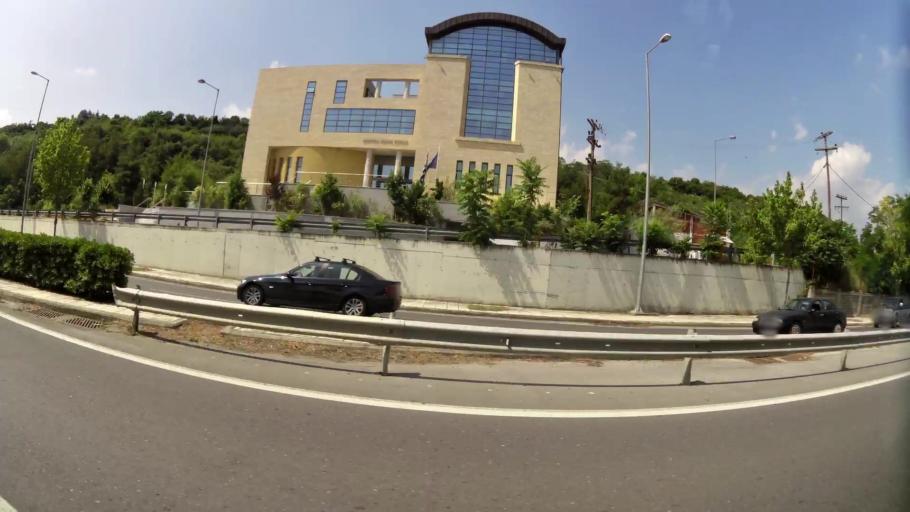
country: GR
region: Central Macedonia
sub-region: Nomos Imathias
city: Veroia
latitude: 40.5081
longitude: 22.2243
